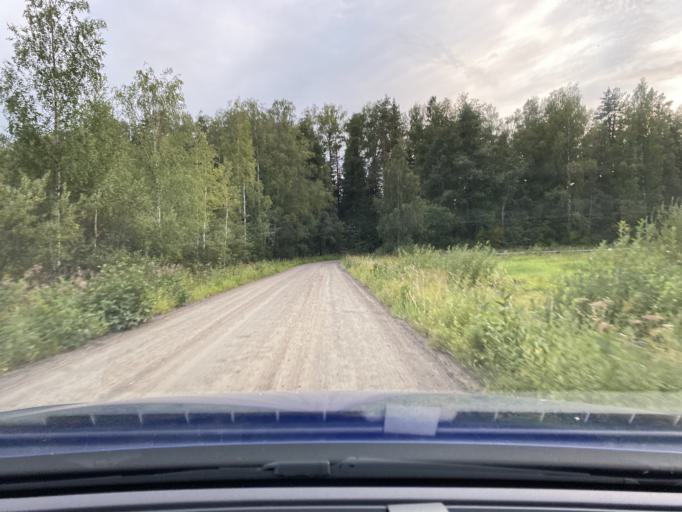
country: FI
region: Pirkanmaa
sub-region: Lounais-Pirkanmaa
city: Punkalaidun
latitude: 61.0616
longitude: 23.2458
